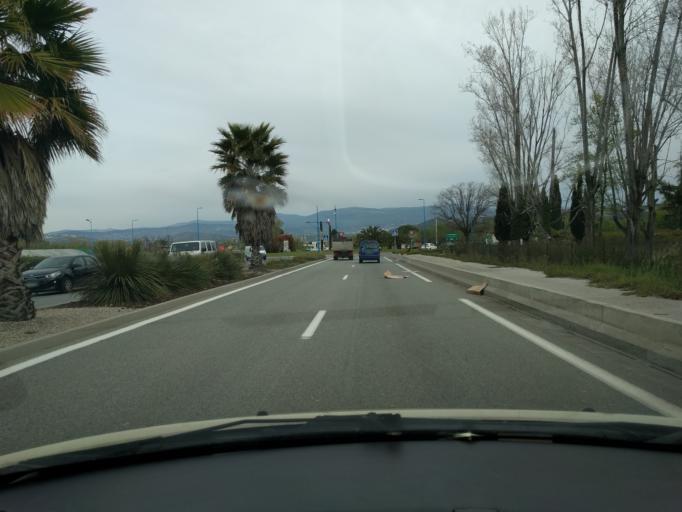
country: FR
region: Provence-Alpes-Cote d'Azur
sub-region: Departement des Alpes-Maritimes
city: Mandelieu-la-Napoule
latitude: 43.5659
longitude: 6.9491
